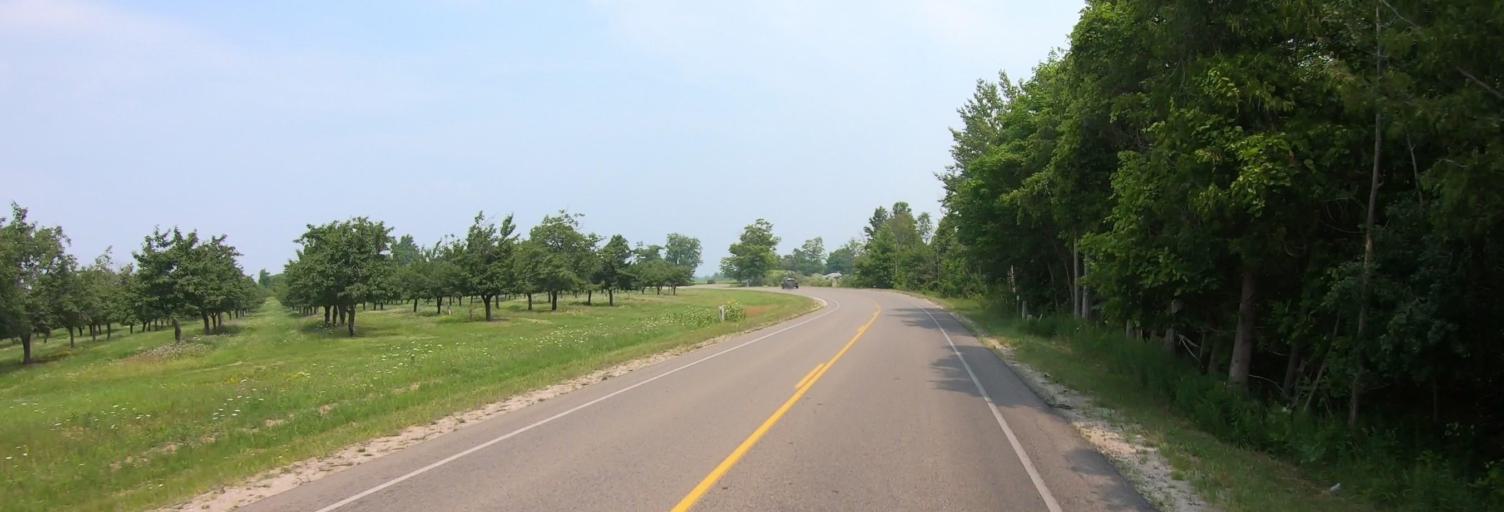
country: US
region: Michigan
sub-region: Leelanau County
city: Leland
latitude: 45.1490
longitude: -85.6117
